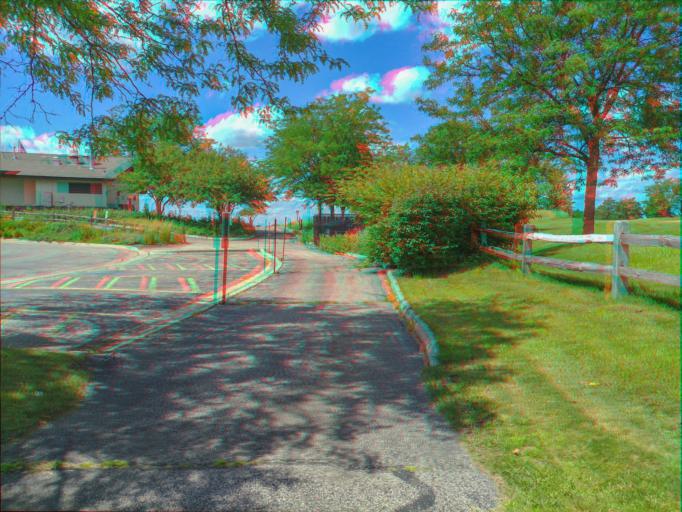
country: US
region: Illinois
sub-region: Lake County
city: Long Grove
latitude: 42.1444
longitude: -87.9972
